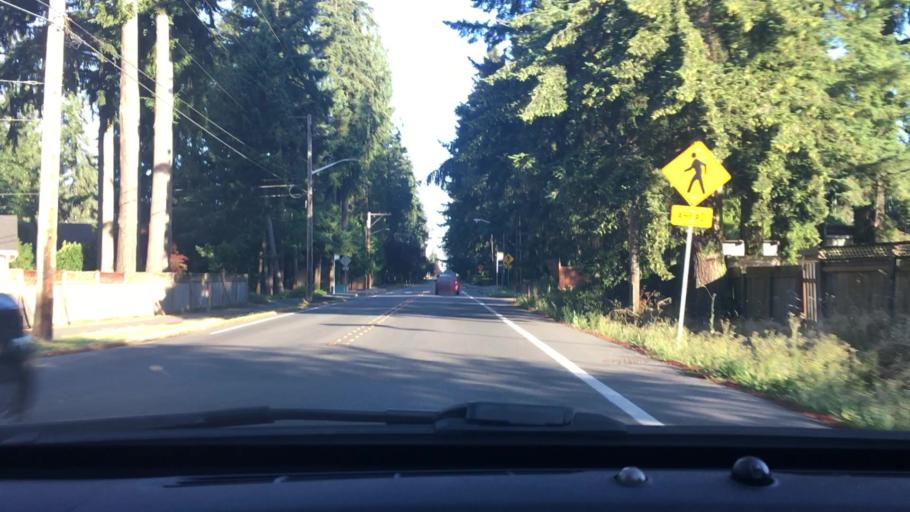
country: US
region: Washington
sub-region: King County
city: Sammamish
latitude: 47.6226
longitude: -122.1158
